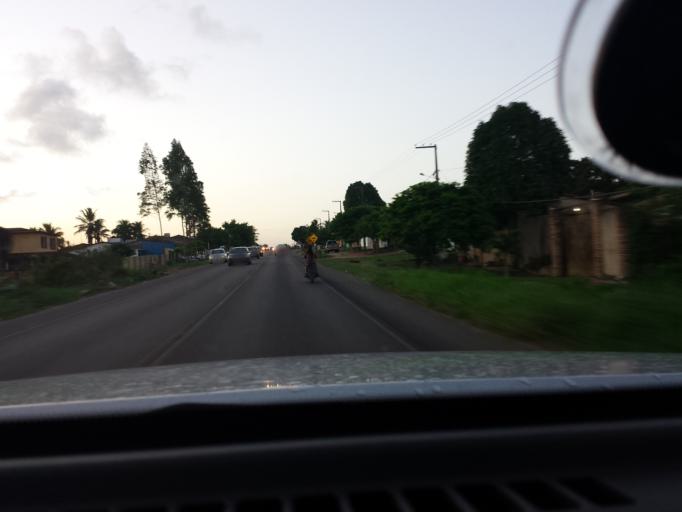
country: BR
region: Sergipe
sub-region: Salgado
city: Salgado
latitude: -11.0035
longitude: -37.5167
